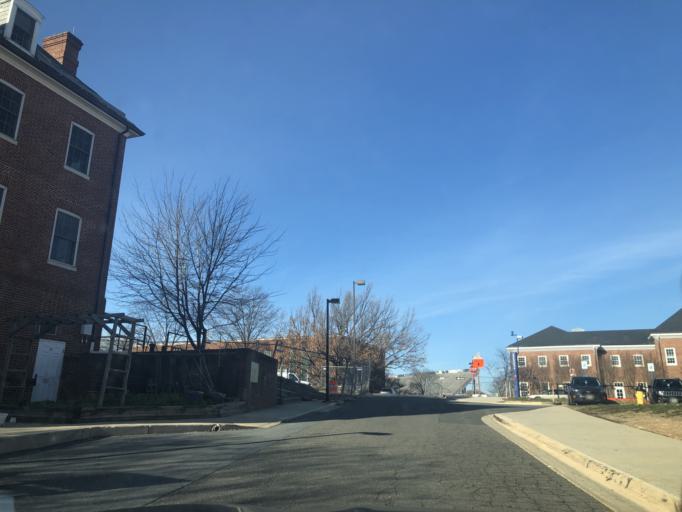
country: US
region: Maryland
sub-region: Prince George's County
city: College Park
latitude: 38.9869
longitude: -76.9452
